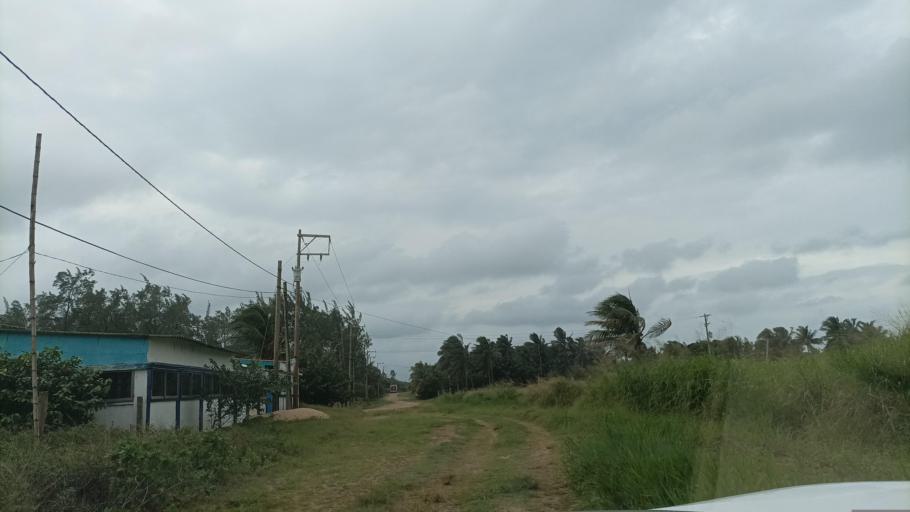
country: MX
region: Veracruz
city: Agua Dulce
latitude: 18.2102
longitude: -94.1381
